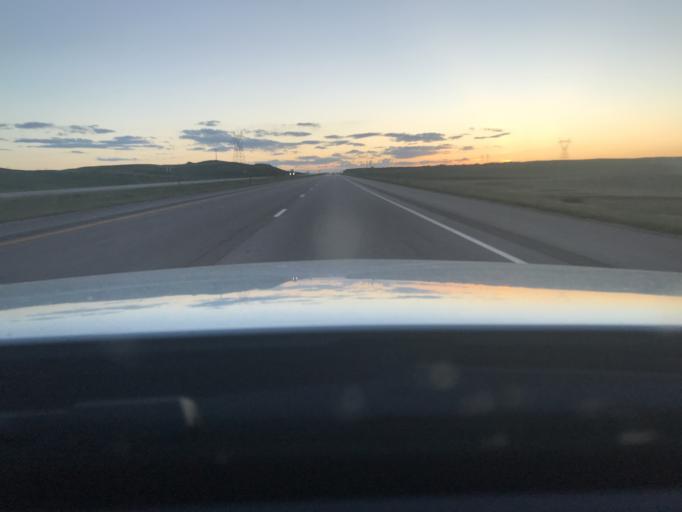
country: US
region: Wyoming
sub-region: Converse County
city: Glenrock
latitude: 42.8204
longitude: -105.7663
